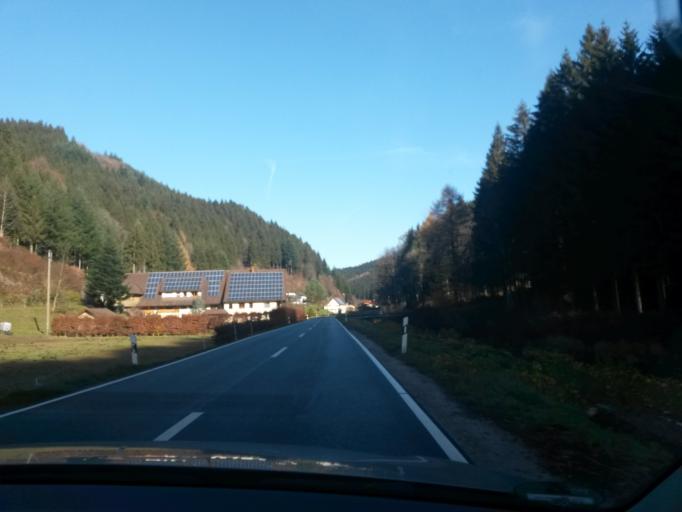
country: DE
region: Baden-Wuerttemberg
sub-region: Freiburg Region
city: Oberwolfach
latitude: 48.3613
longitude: 8.2713
